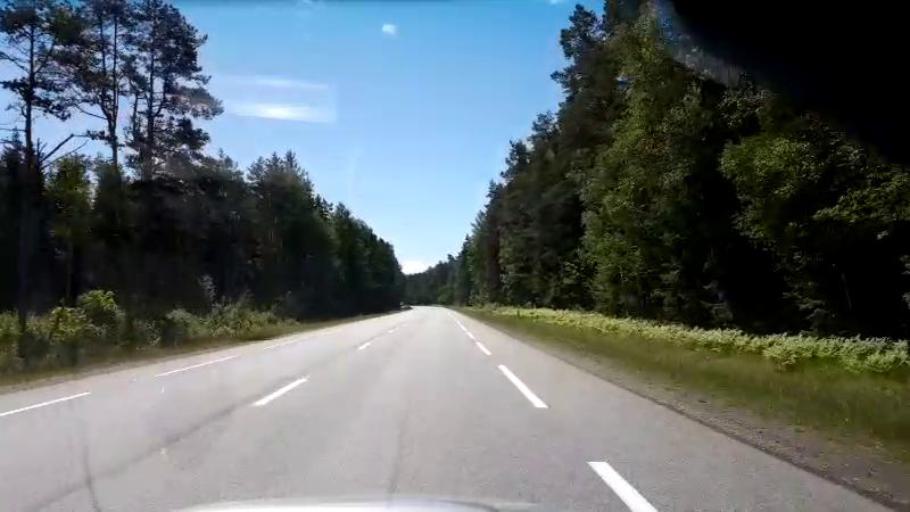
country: LV
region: Saulkrastu
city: Saulkrasti
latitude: 57.4523
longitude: 24.4301
